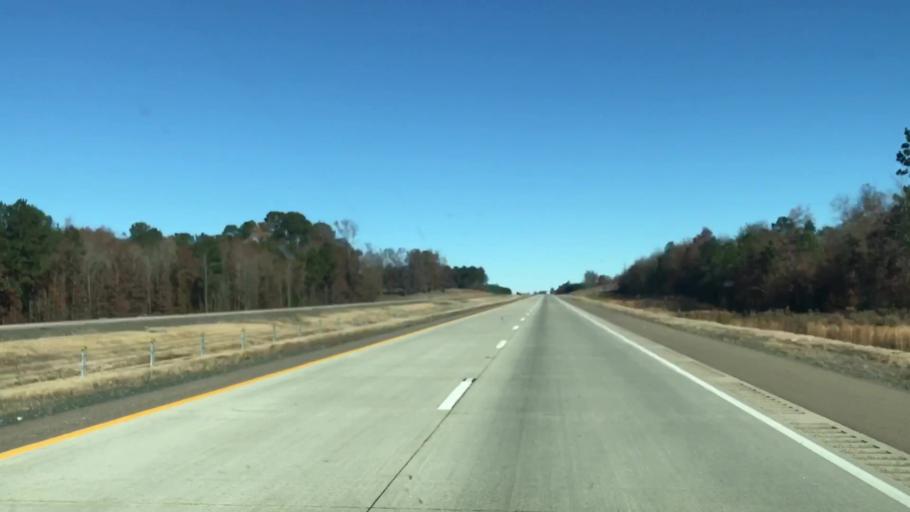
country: US
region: Louisiana
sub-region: Caddo Parish
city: Vivian
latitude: 33.0364
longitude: -93.9007
